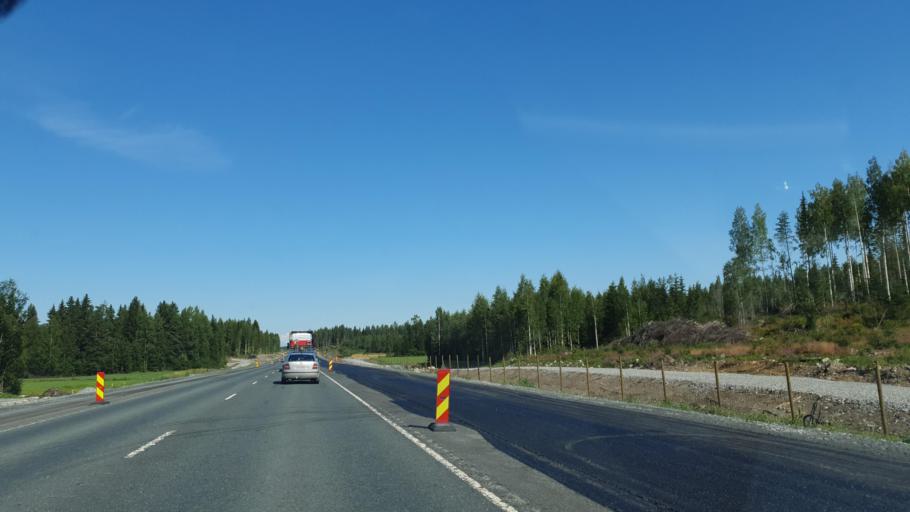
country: FI
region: Northern Savo
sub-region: Ylae-Savo
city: Lapinlahti
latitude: 63.2963
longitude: 27.4528
